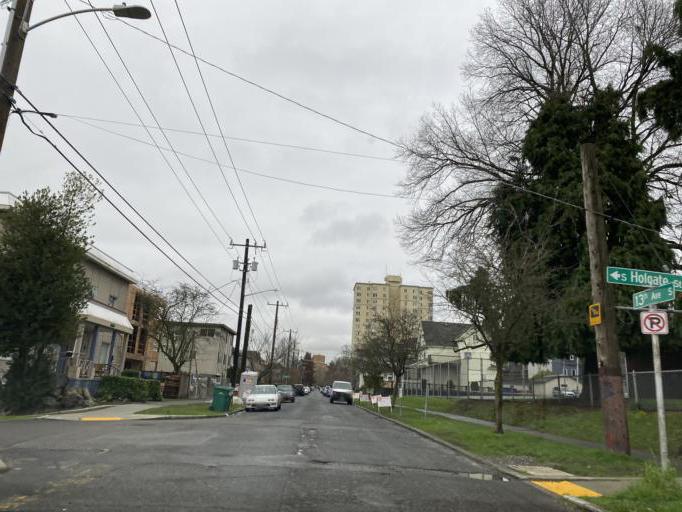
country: US
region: Washington
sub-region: King County
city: Seattle
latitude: 47.5863
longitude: -122.3160
